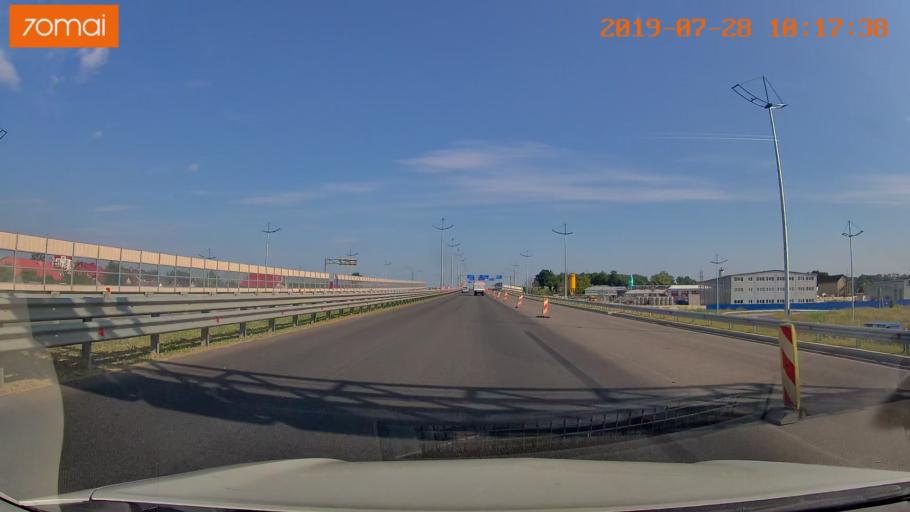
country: RU
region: Kaliningrad
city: Maloye Isakovo
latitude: 54.7423
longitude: 20.5933
